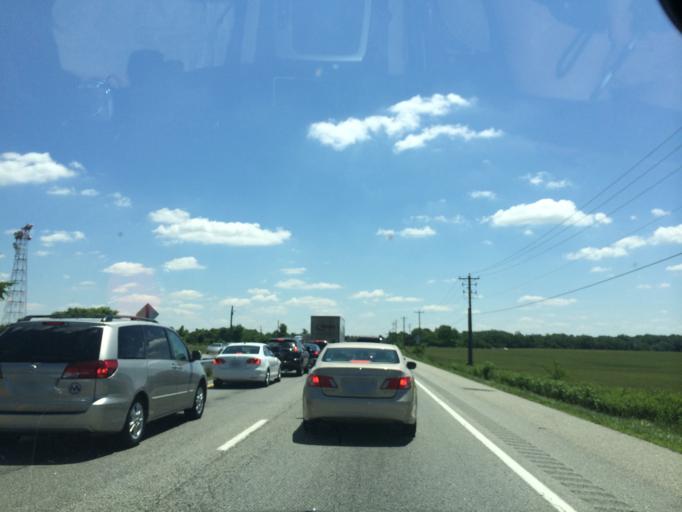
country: US
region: Maryland
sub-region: Queen Anne's County
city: Centreville
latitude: 38.9552
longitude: -76.0822
